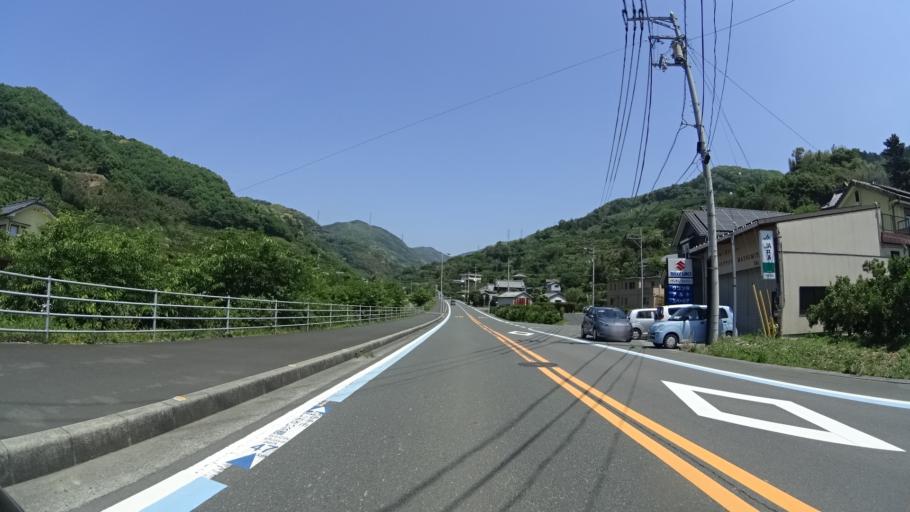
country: JP
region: Ehime
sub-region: Nishiuwa-gun
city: Ikata-cho
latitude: 33.4958
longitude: 132.3971
